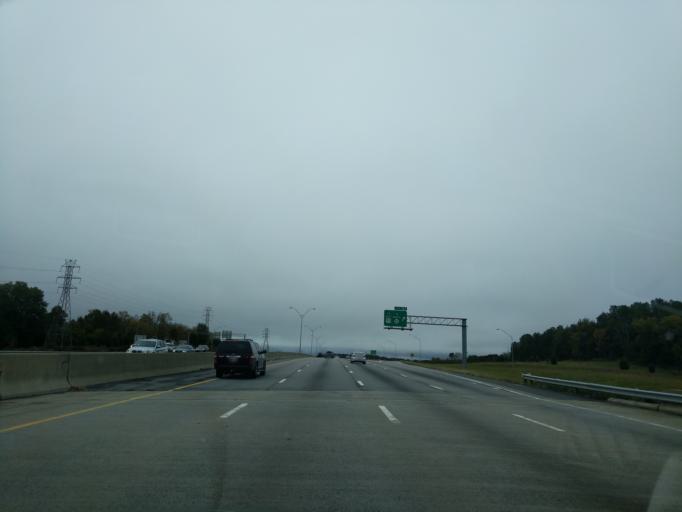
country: US
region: North Carolina
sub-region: Orange County
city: Hillsborough
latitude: 36.0735
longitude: -79.1700
